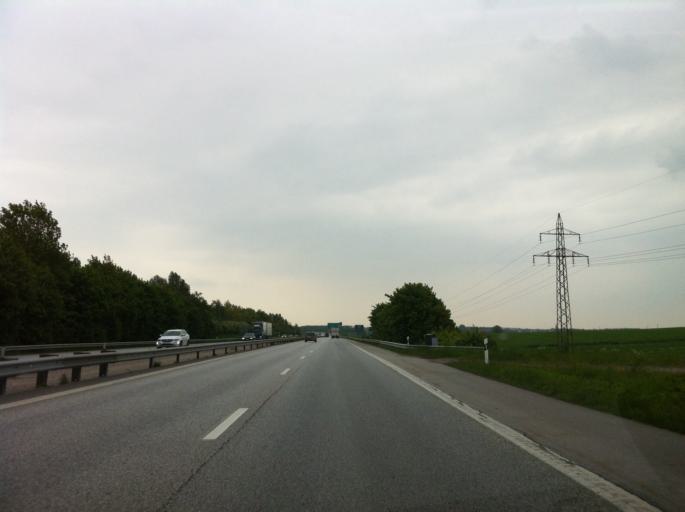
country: SE
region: Skane
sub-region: Lomma Kommun
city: Lomma
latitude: 55.6637
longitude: 13.0993
